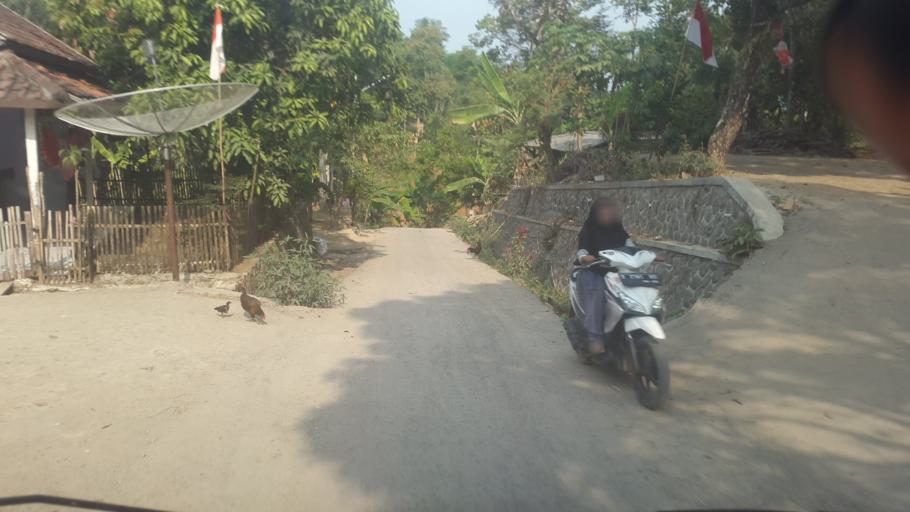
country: ID
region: West Java
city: Pelabuhanratu
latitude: -6.9417
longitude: 106.5452
